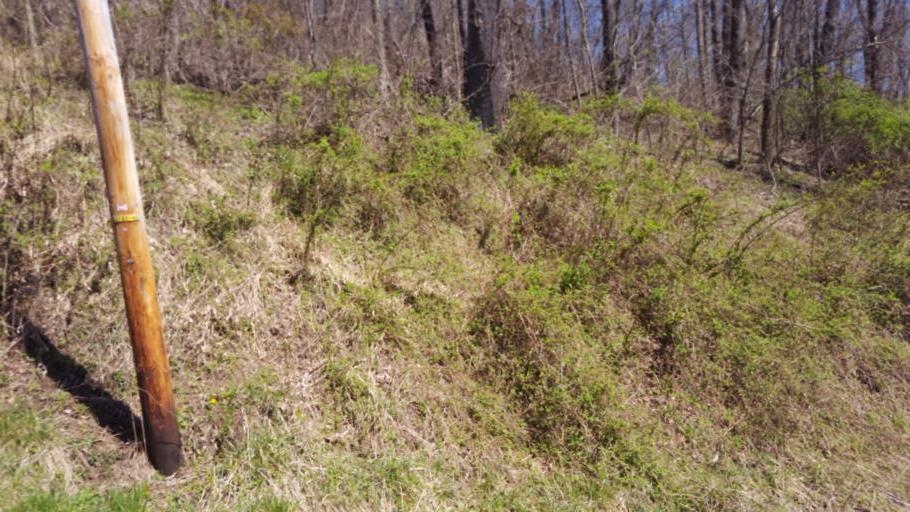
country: US
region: Ohio
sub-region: Belmont County
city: Martins Ferry
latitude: 40.1046
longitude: -80.7271
